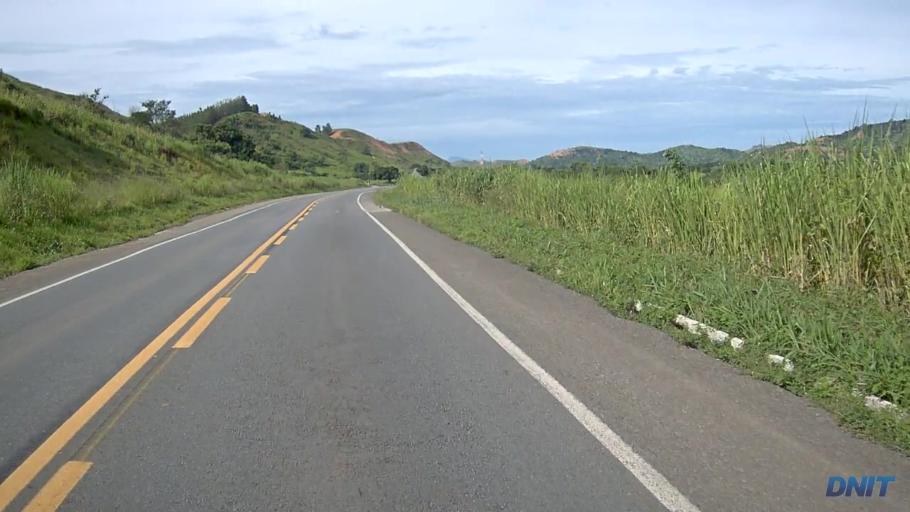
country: BR
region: Minas Gerais
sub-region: Belo Oriente
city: Belo Oriente
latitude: -19.1832
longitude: -42.2630
